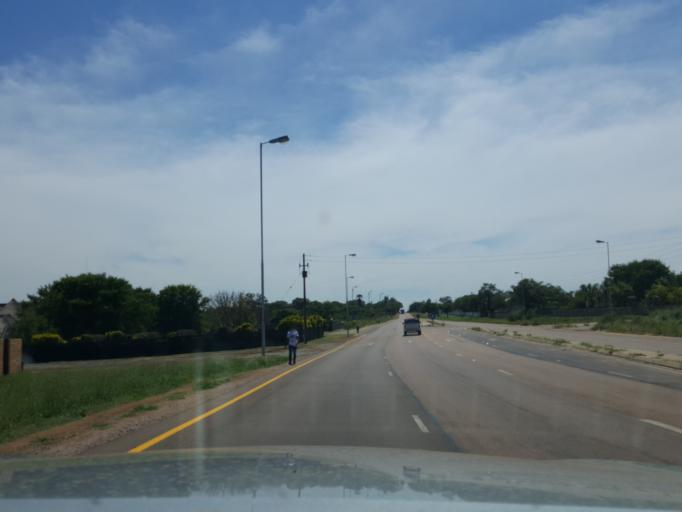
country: ZA
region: Gauteng
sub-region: City of Tshwane Metropolitan Municipality
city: Pretoria
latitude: -25.6816
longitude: 28.2990
